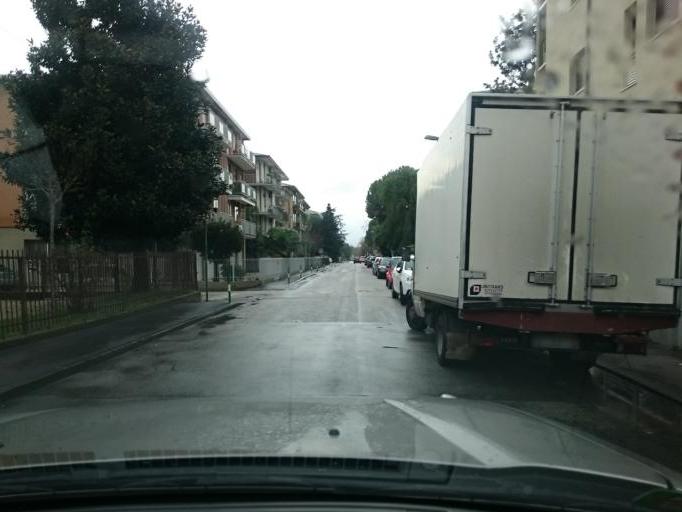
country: IT
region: Veneto
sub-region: Provincia di Padova
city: Padova
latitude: 45.4266
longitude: 11.8851
